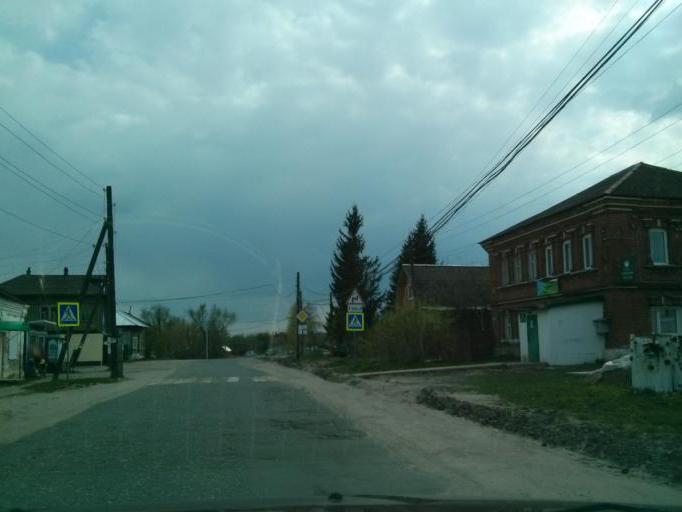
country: RU
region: Nizjnij Novgorod
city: Shimorskoye
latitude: 55.3351
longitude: 41.9282
